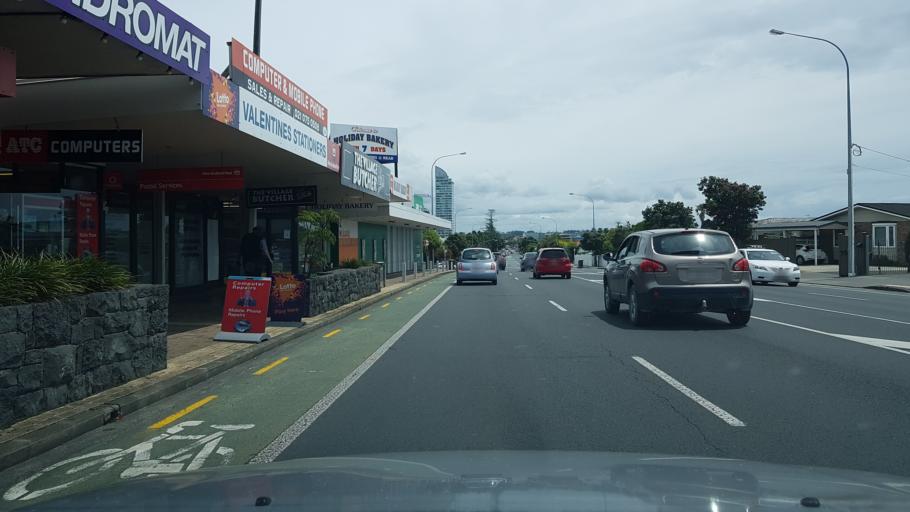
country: NZ
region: Auckland
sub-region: Auckland
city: North Shore
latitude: -36.7971
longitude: 174.7786
